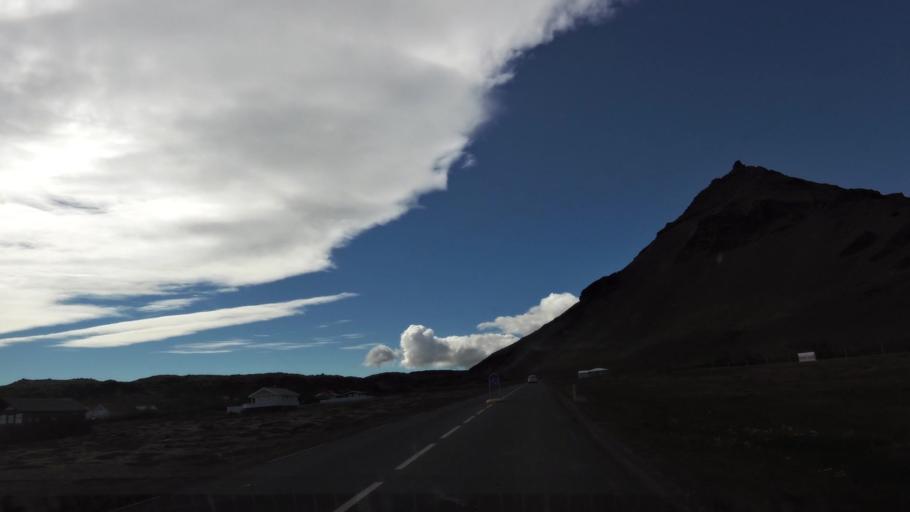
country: IS
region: West
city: Olafsvik
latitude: 64.7663
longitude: -23.6351
